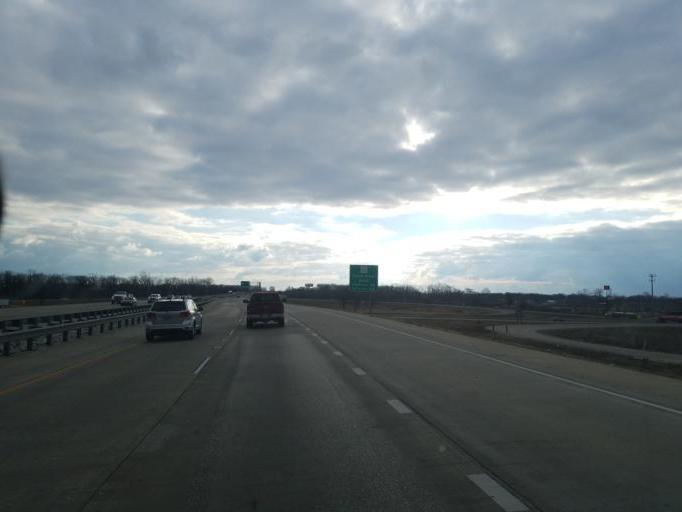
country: US
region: Illinois
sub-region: Madison County
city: Mitchell
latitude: 38.7659
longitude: -90.1267
